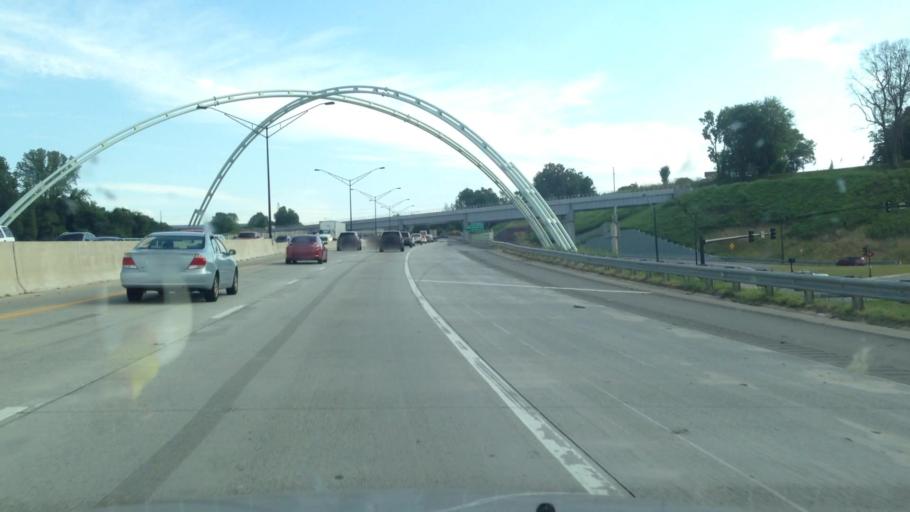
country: US
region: North Carolina
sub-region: Forsyth County
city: Winston-Salem
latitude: 36.0850
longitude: -80.2292
